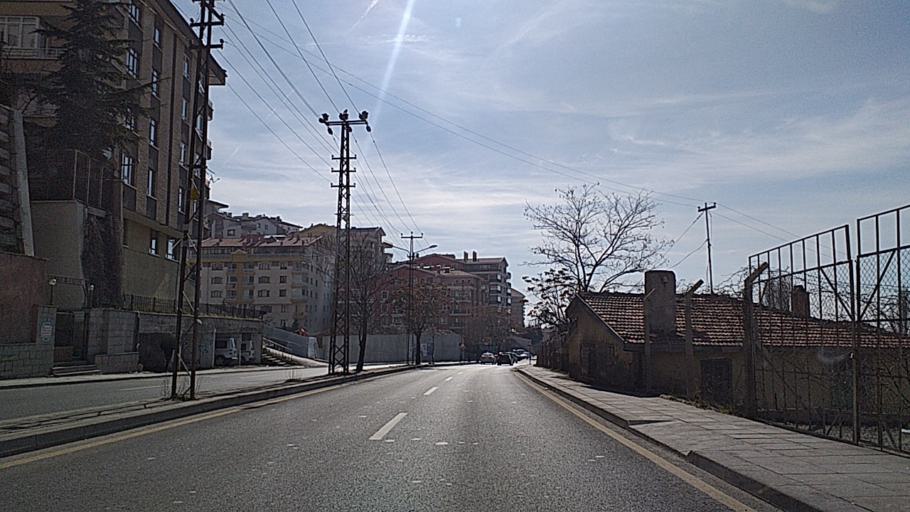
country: TR
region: Ankara
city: Ankara
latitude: 39.9866
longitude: 32.8222
